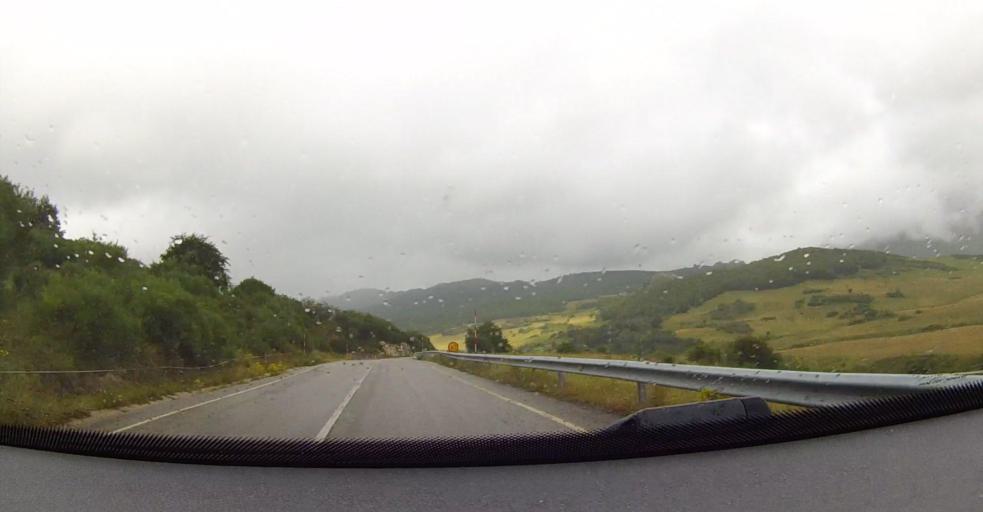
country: ES
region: Castille and Leon
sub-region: Provincia de Leon
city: Marana
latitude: 43.0720
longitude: -5.2036
